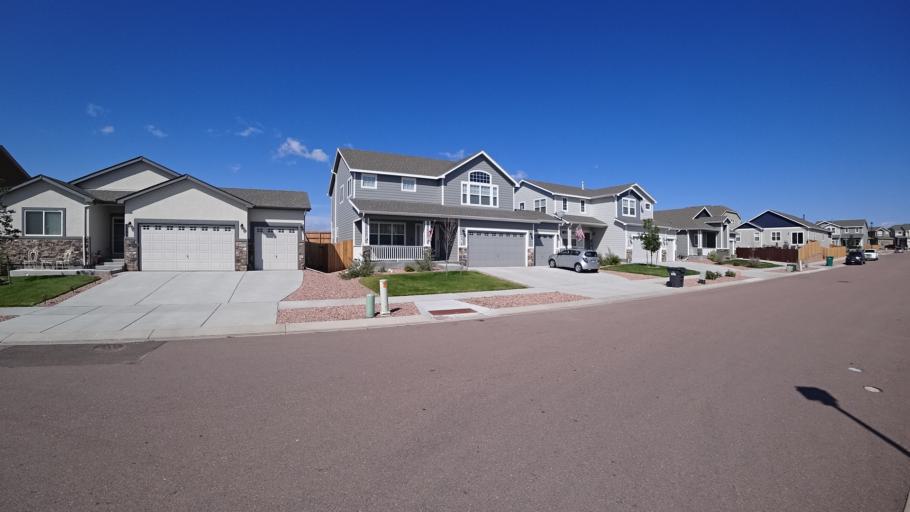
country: US
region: Colorado
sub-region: El Paso County
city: Cimarron Hills
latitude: 38.9313
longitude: -104.7098
